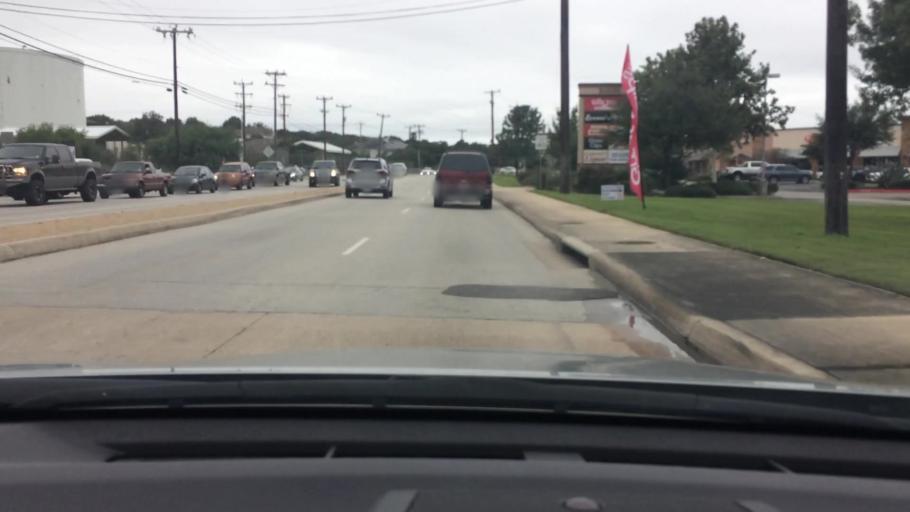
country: US
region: Texas
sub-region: Bexar County
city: Hollywood Park
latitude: 29.6479
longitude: -98.4256
